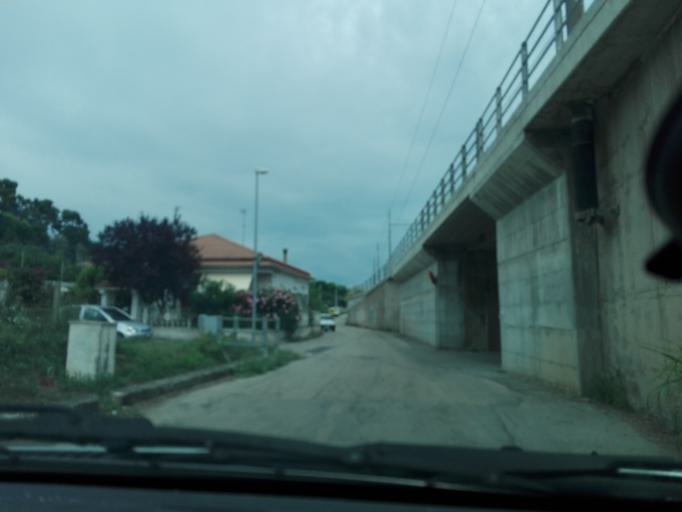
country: IT
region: Abruzzo
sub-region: Provincia di Pescara
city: Montesilvano Marina
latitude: 42.5006
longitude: 14.1644
